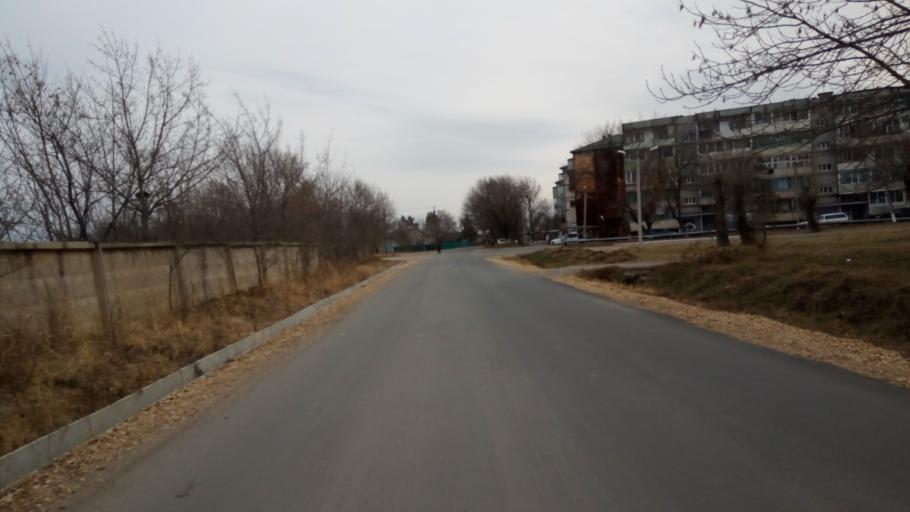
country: RU
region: Primorskiy
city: Novoshakhtinskiy
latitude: 44.0291
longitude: 132.1710
